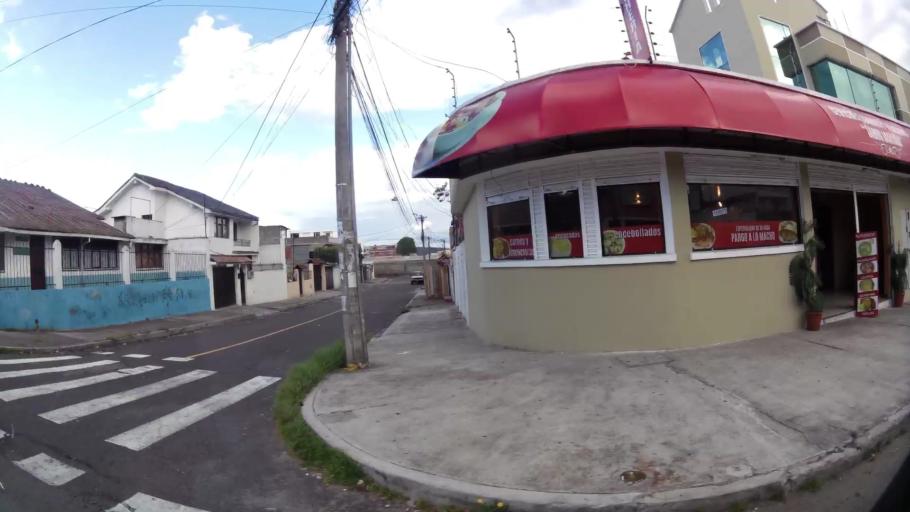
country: EC
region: Pichincha
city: Quito
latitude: -0.1377
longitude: -78.4779
